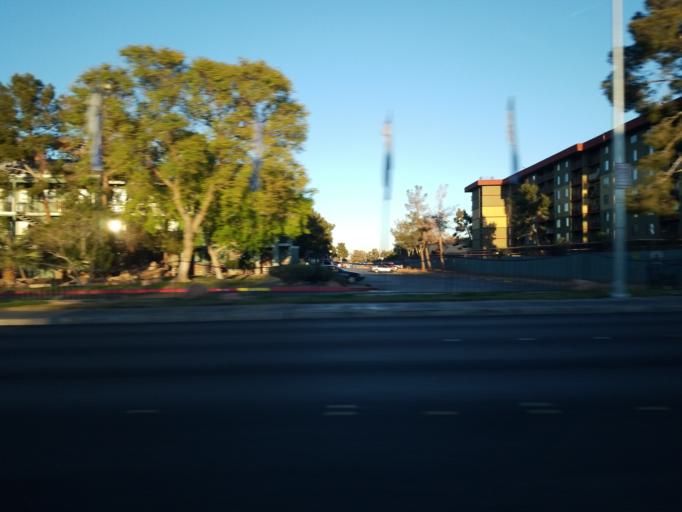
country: US
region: Nevada
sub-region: Clark County
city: Paradise
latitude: 36.1204
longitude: -115.1462
